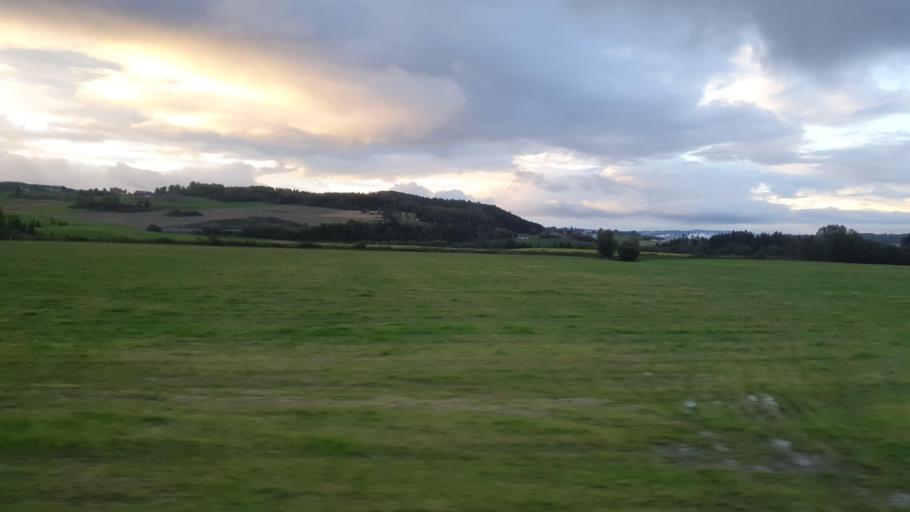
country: NO
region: Nord-Trondelag
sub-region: Levanger
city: Skogn
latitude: 63.6771
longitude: 11.1443
